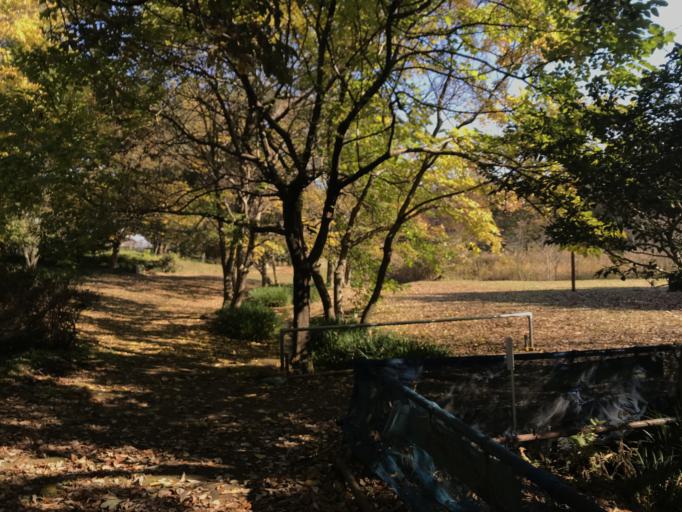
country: JP
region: Saitama
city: Tokorozawa
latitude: 35.7884
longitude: 139.5213
